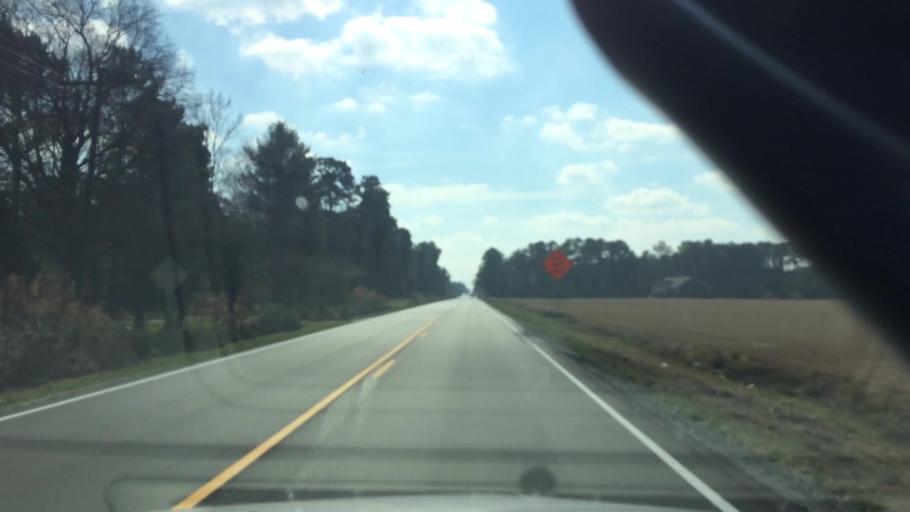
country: US
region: North Carolina
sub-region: Duplin County
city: Beulaville
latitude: 35.0279
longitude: -77.7485
